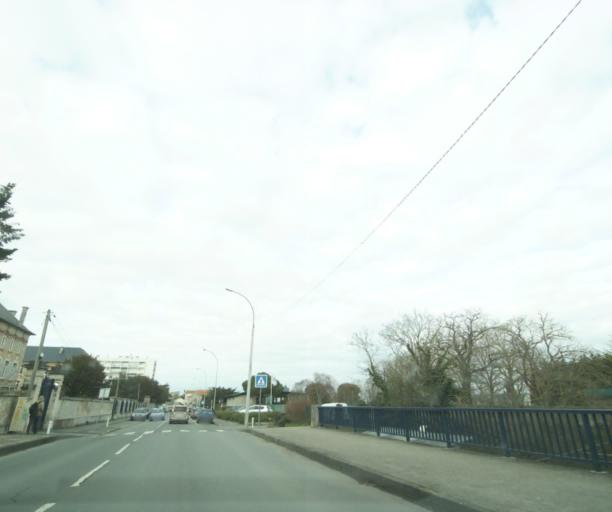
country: FR
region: Poitou-Charentes
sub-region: Departement de la Charente-Maritime
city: La Rochelle
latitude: 46.1652
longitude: -1.1645
